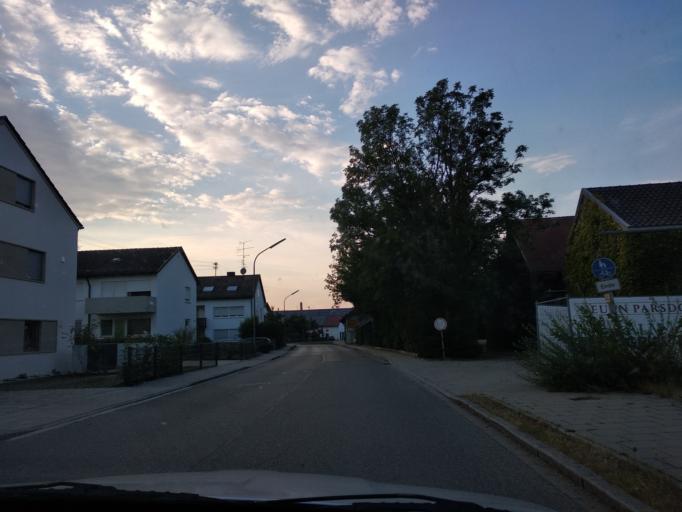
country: DE
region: Bavaria
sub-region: Upper Bavaria
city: Vaterstetten
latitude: 48.1400
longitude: 11.7876
